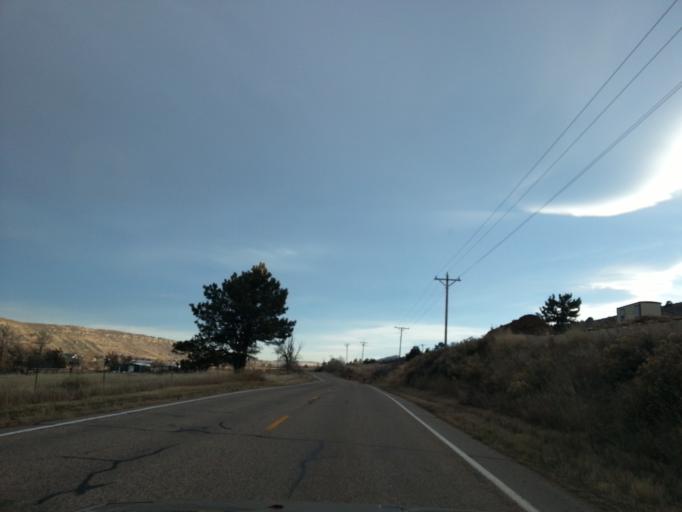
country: US
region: Colorado
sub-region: Larimer County
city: Loveland
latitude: 40.4746
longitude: -105.2134
